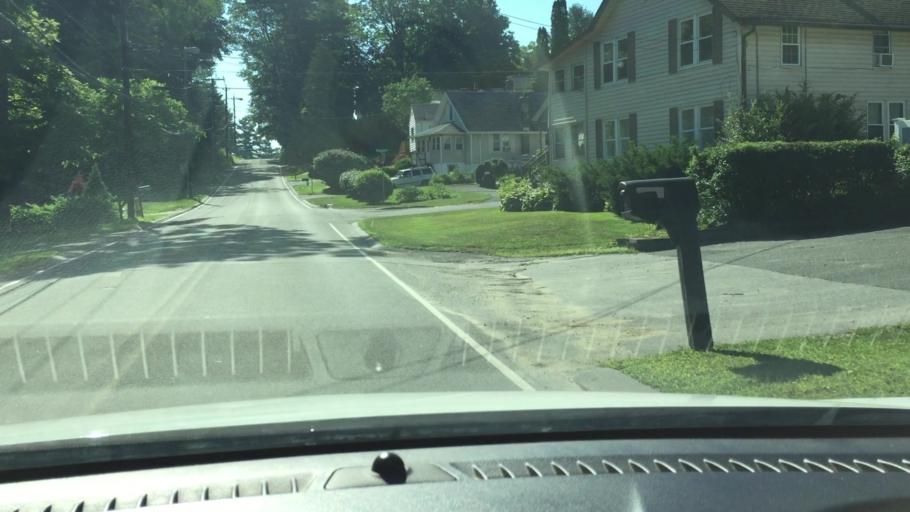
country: US
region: Massachusetts
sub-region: Berkshire County
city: Pittsfield
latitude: 42.4862
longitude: -73.2535
